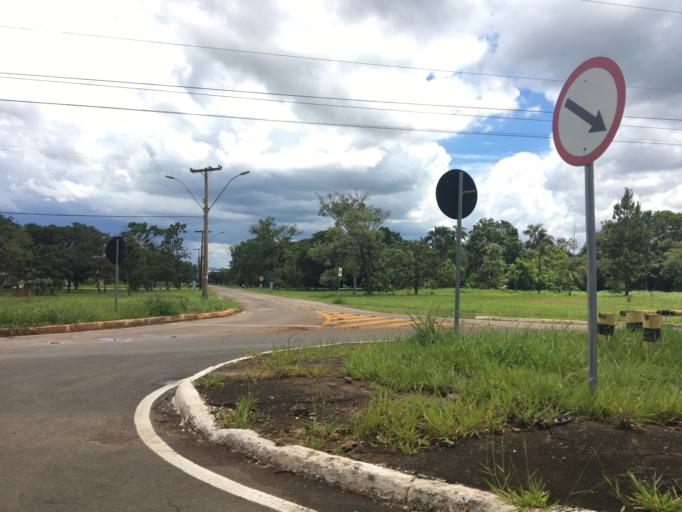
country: BR
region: Federal District
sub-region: Brasilia
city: Brasilia
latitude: -15.8991
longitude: -47.9269
